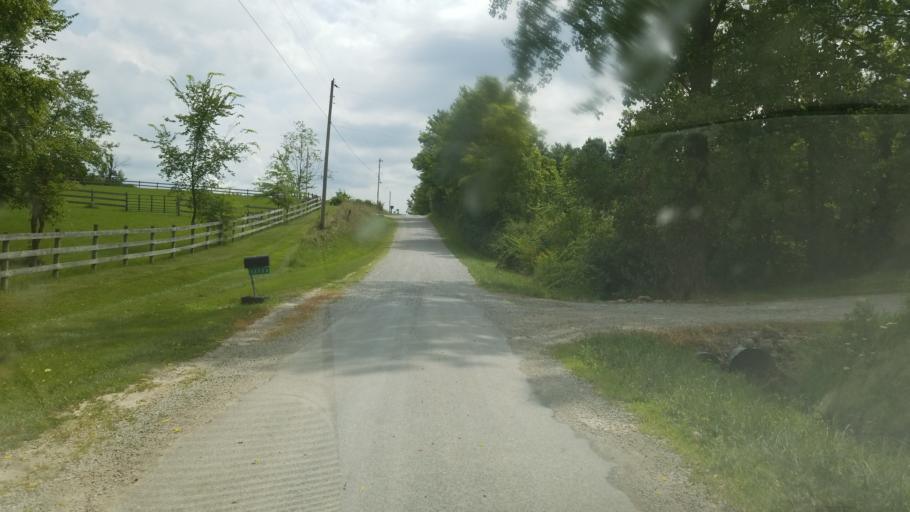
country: US
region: Ohio
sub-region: Delaware County
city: Sunbury
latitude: 40.3256
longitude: -82.8098
